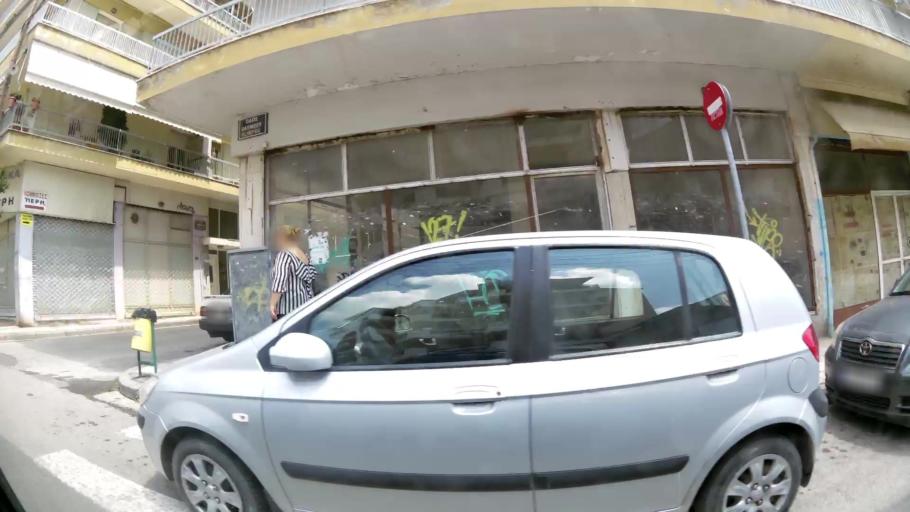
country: GR
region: West Macedonia
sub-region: Nomos Kozanis
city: Kozani
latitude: 40.2981
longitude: 21.7909
